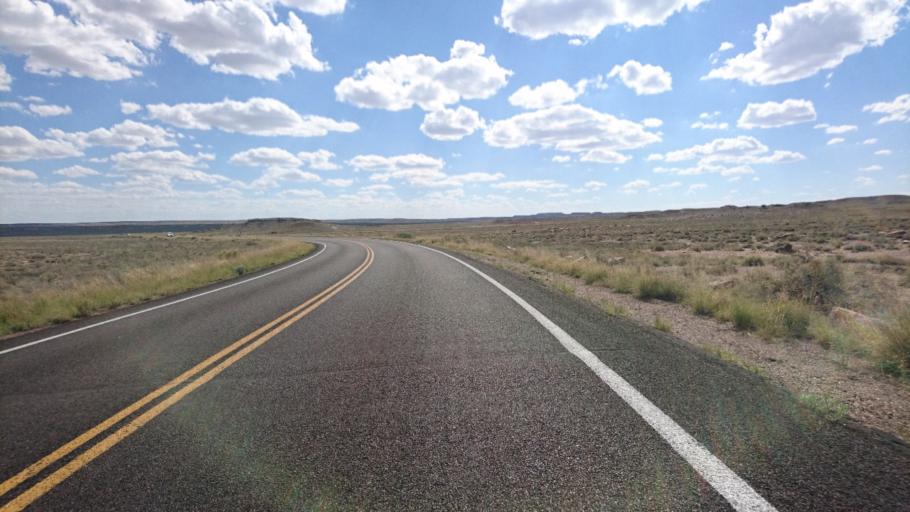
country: US
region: Arizona
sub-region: Navajo County
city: Holbrook
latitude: 34.8896
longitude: -109.8031
